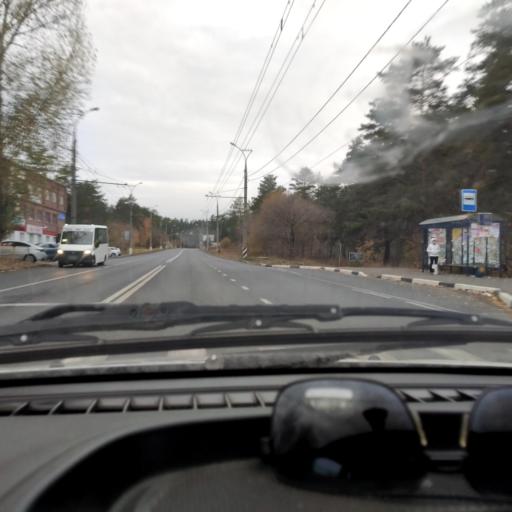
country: RU
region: Samara
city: Zhigulevsk
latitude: 53.4871
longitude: 49.4705
